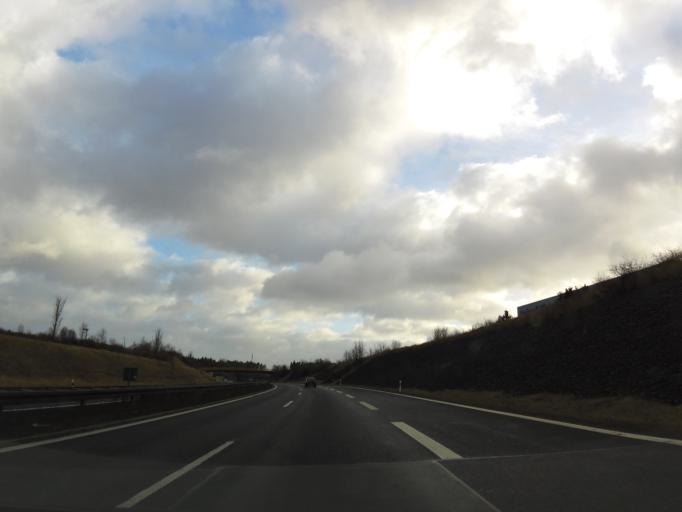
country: DE
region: Bavaria
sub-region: Upper Franconia
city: Hochstadt bei Thiersheim
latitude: 50.1023
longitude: 12.0948
